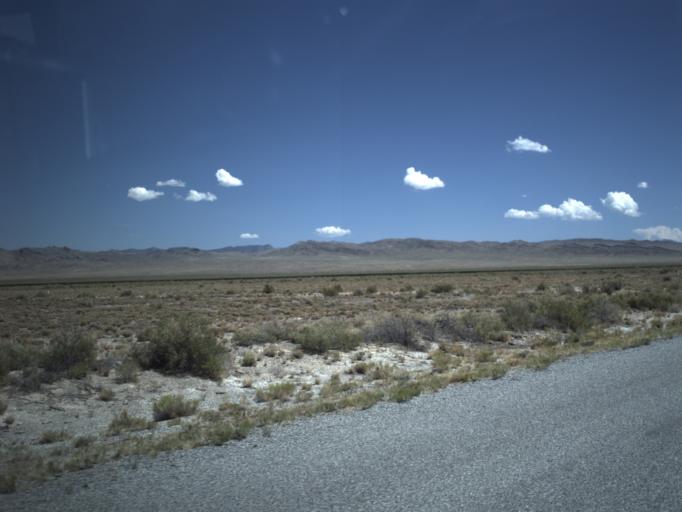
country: US
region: Nevada
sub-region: White Pine County
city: McGill
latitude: 39.0509
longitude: -113.9670
